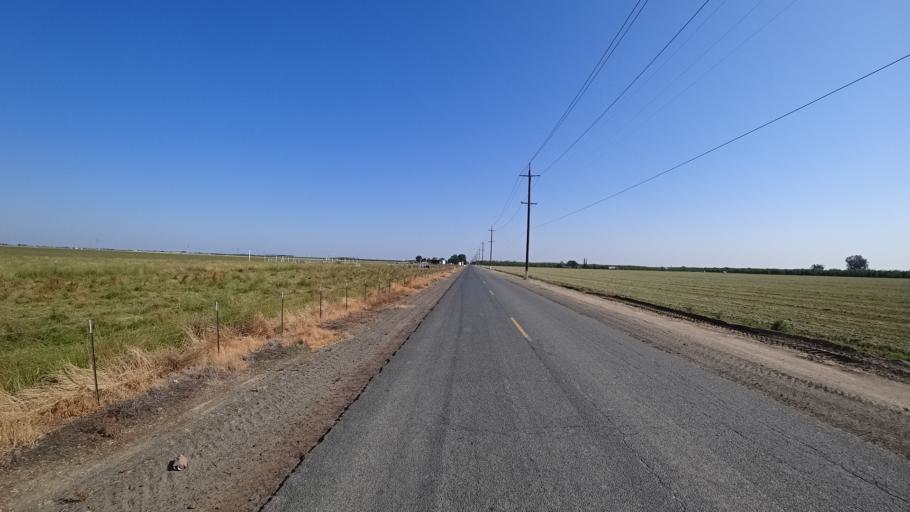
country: US
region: California
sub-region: Kings County
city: Home Garden
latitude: 36.2643
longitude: -119.5831
